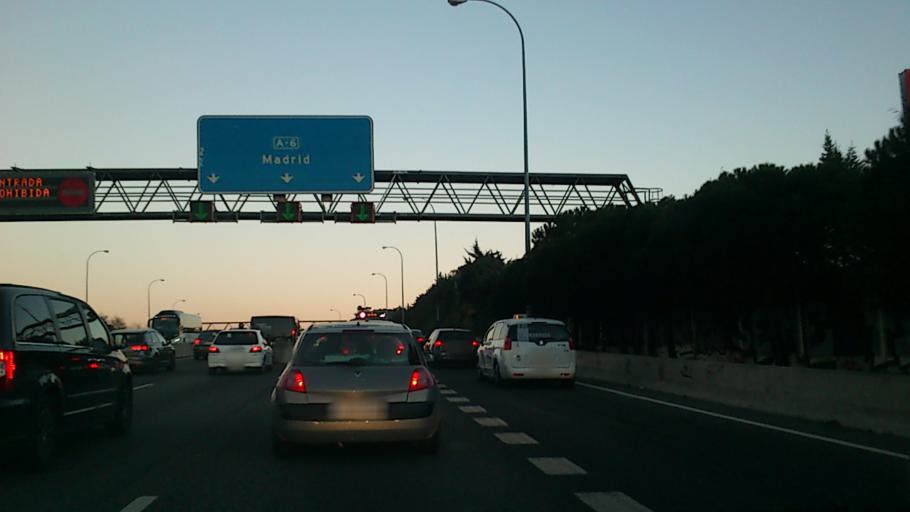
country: ES
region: Madrid
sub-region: Provincia de Madrid
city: Majadahonda
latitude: 40.4766
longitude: -3.8412
